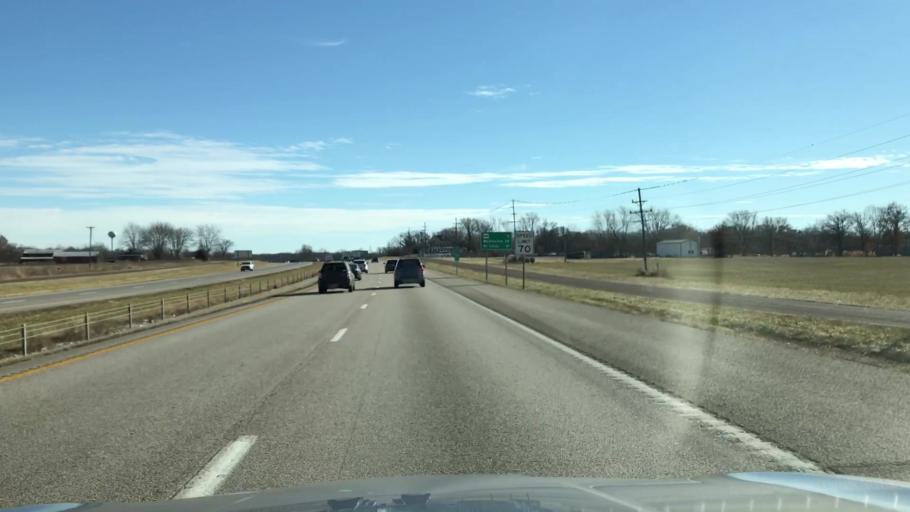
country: US
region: Missouri
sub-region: Warren County
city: Warrenton
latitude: 38.8323
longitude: -91.2172
